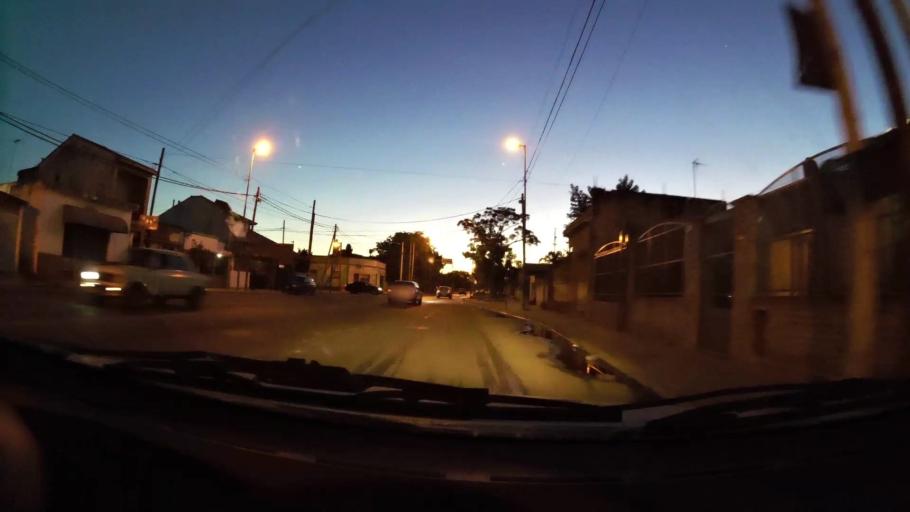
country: AR
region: Buenos Aires
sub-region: Partido de Quilmes
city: Quilmes
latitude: -34.7751
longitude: -58.1885
